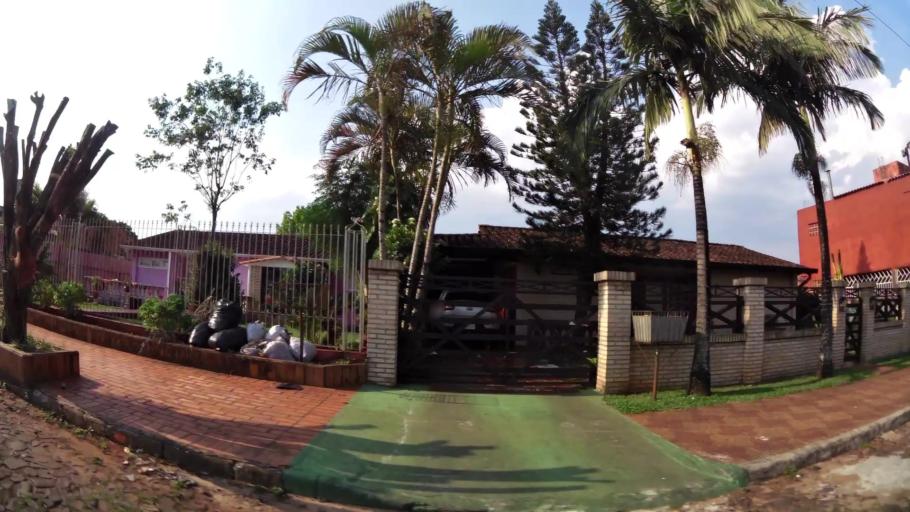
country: PY
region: Alto Parana
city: Presidente Franco
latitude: -25.5339
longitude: -54.6286
